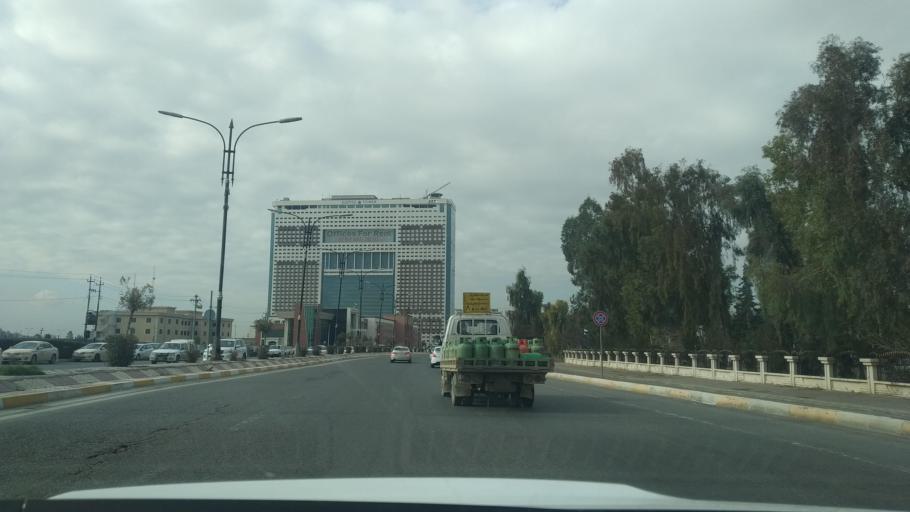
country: IQ
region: Arbil
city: Erbil
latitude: 36.1846
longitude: 43.9845
